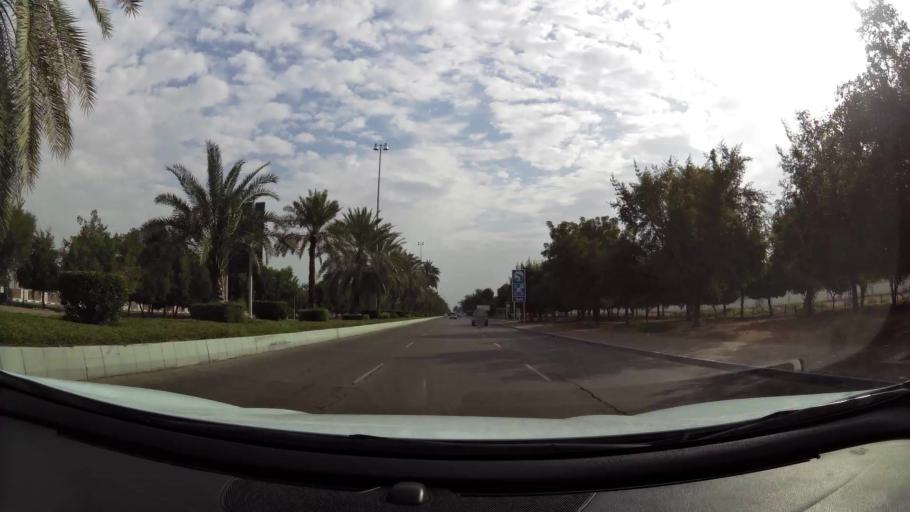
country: AE
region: Abu Dhabi
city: Al Ain
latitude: 24.2058
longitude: 55.6822
